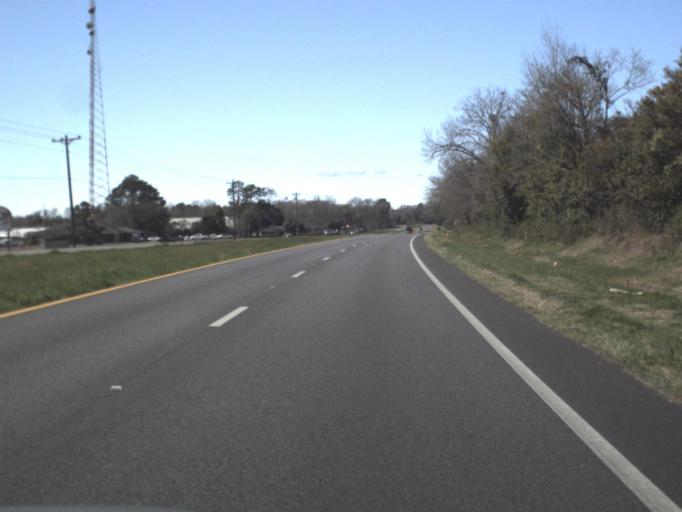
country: US
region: Florida
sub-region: Gadsden County
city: Quincy
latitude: 30.5857
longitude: -84.6167
